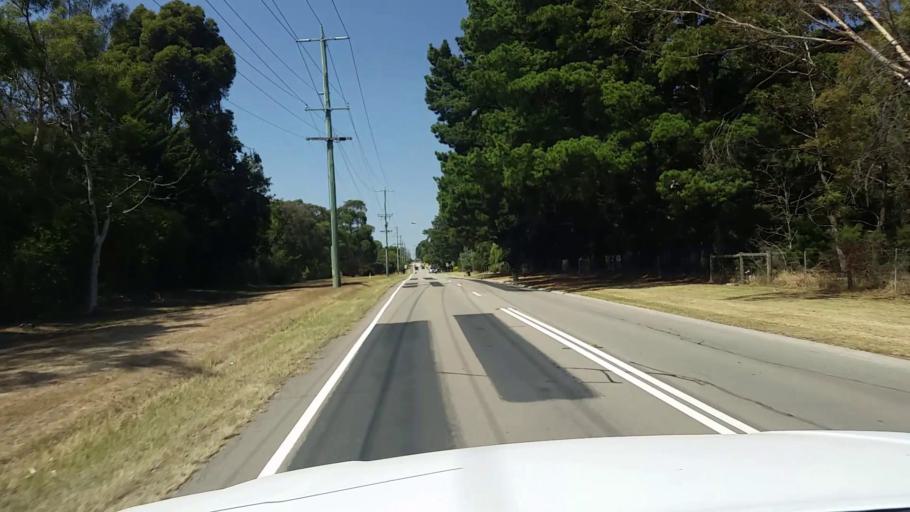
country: AU
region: Victoria
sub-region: Mornington Peninsula
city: Somerville
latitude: -38.2365
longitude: 145.1591
